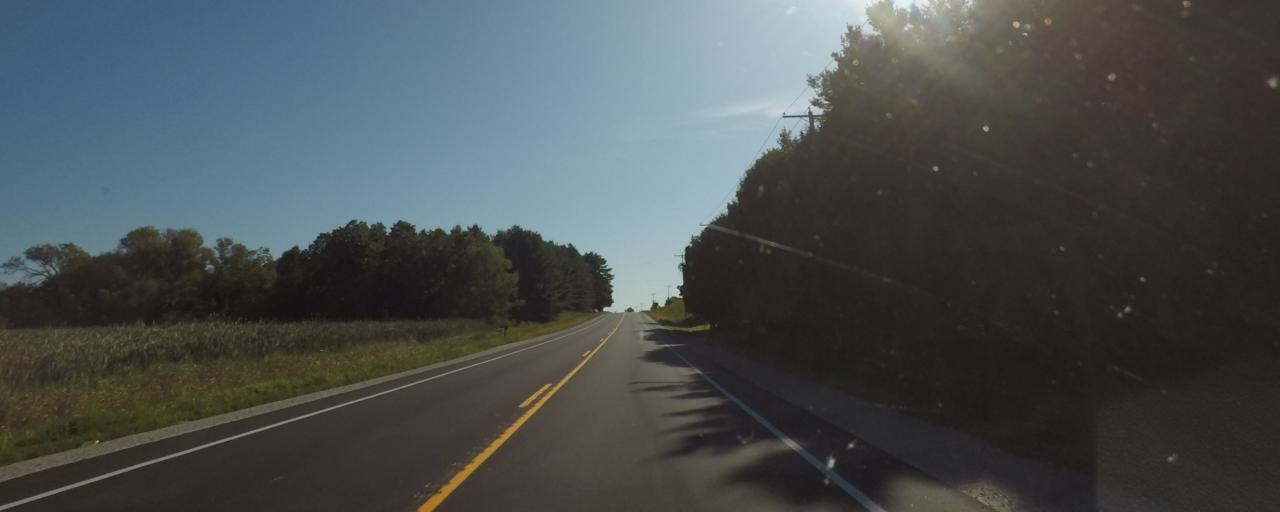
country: US
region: Wisconsin
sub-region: Jefferson County
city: Johnson Creek
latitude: 43.0143
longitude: -88.6837
